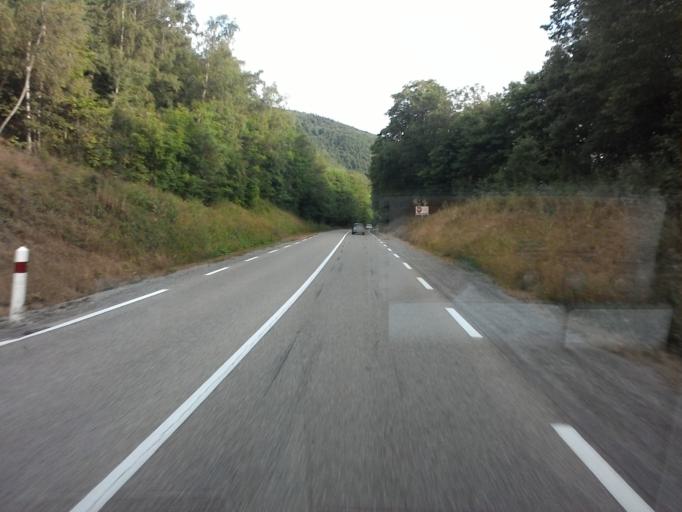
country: FR
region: Rhone-Alpes
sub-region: Departement de l'Isere
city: Pierre-Chatel
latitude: 44.9688
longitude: 5.7743
